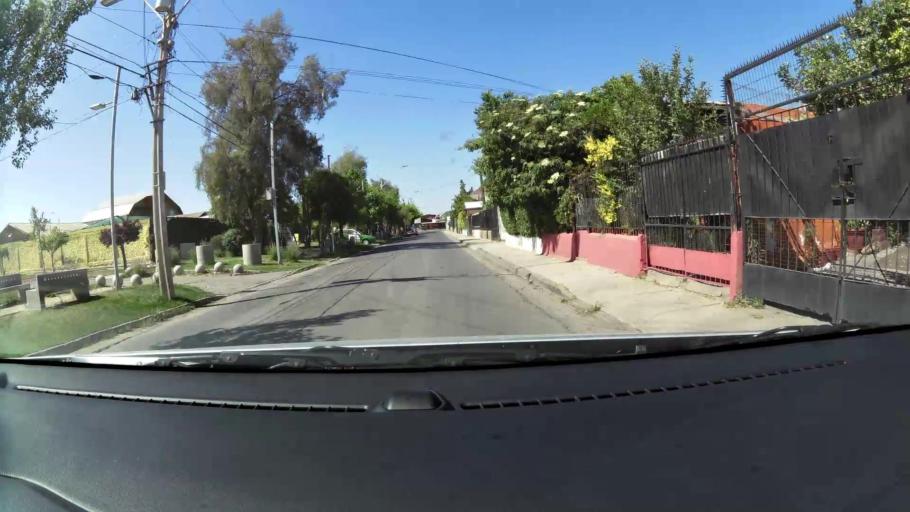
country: CL
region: Santiago Metropolitan
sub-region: Provincia de Santiago
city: La Pintana
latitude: -33.5539
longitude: -70.6543
